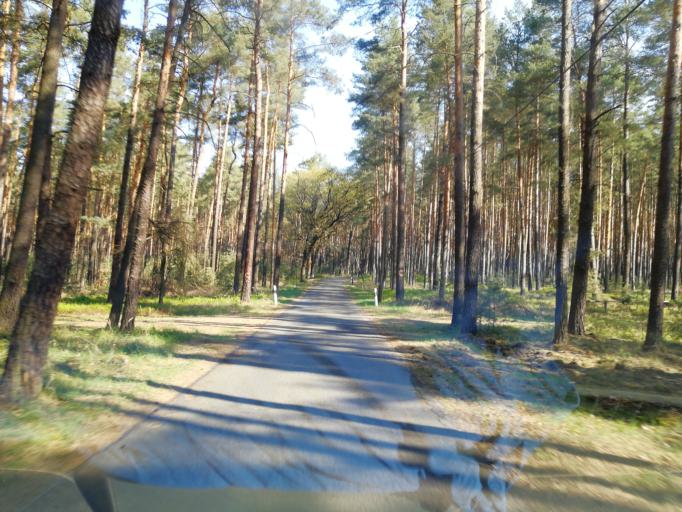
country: DE
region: Brandenburg
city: Bronkow
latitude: 51.6835
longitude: 13.8645
